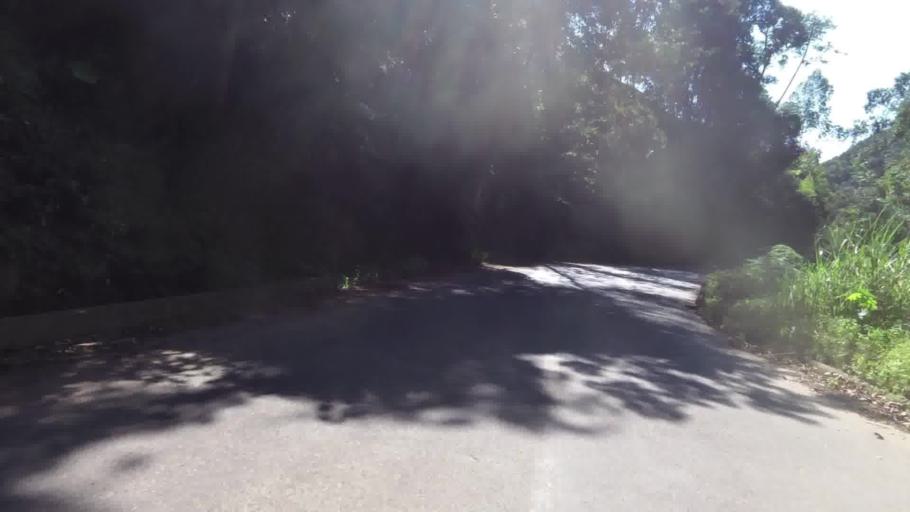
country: BR
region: Espirito Santo
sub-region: Marechal Floriano
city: Marechal Floriano
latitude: -20.4533
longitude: -40.8941
